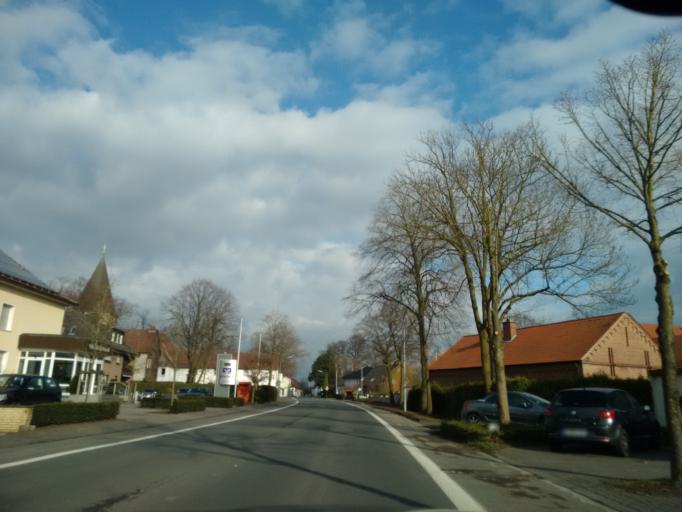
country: DE
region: North Rhine-Westphalia
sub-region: Regierungsbezirk Arnsberg
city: Lippstadt
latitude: 51.6894
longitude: 8.4319
